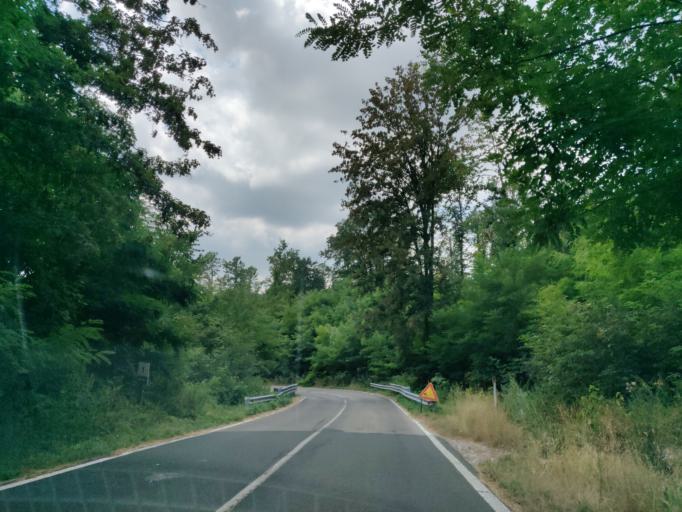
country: IT
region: Tuscany
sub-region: Provincia di Siena
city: Abbadia San Salvatore
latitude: 42.8856
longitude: 11.6570
